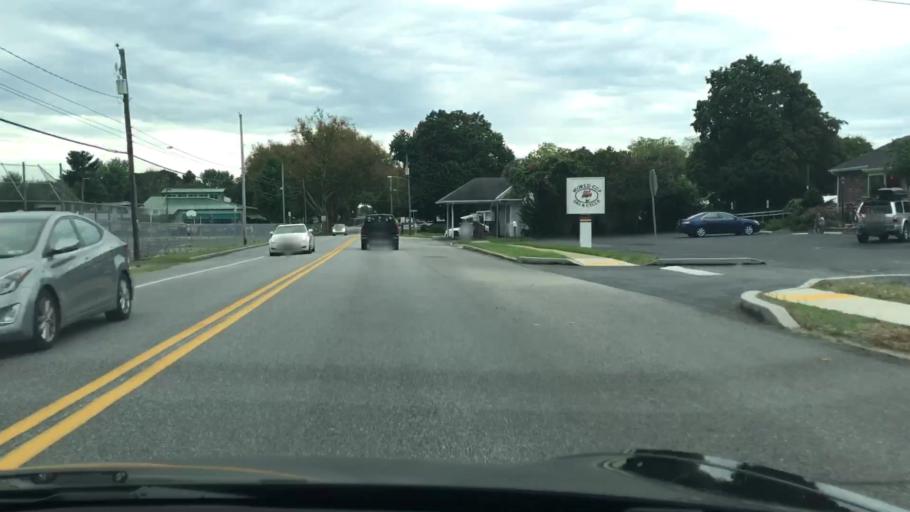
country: US
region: Pennsylvania
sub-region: Cumberland County
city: Shiremanstown
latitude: 40.2222
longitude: -76.9413
